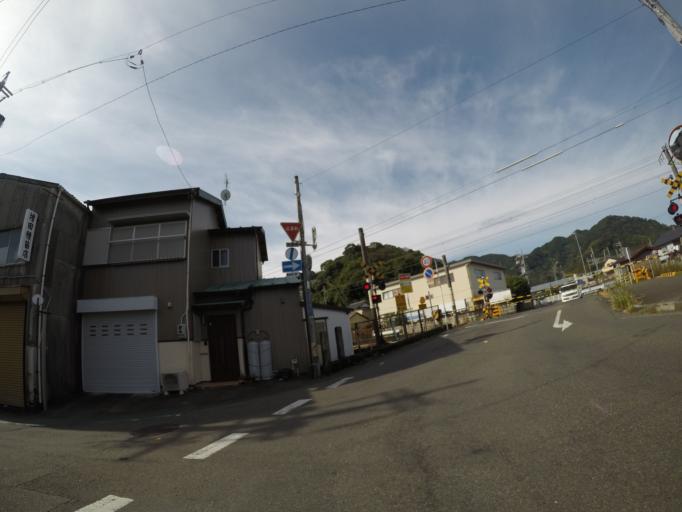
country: JP
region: Shizuoka
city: Shizuoka-shi
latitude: 34.9255
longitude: 138.3628
